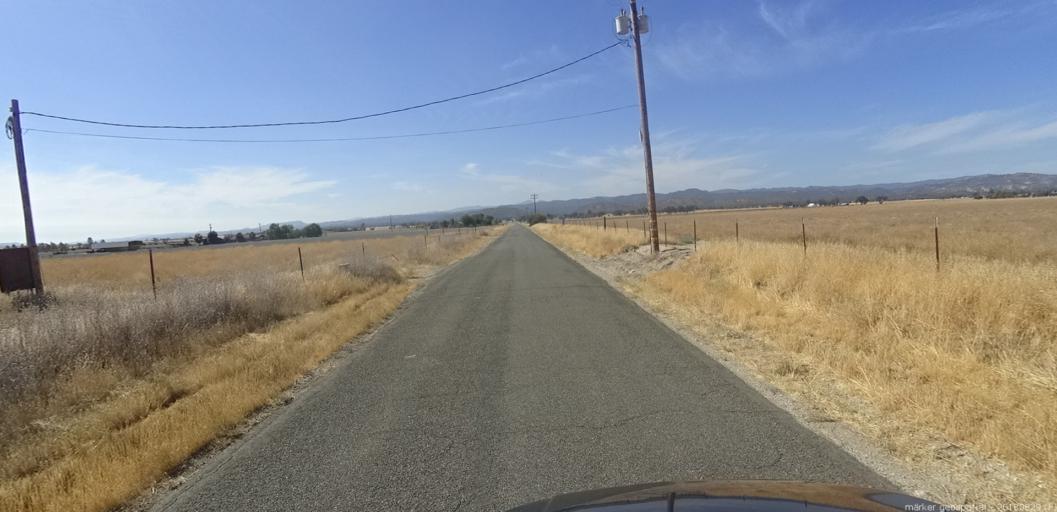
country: US
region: California
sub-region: Monterey County
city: King City
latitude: 35.9577
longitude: -121.0819
